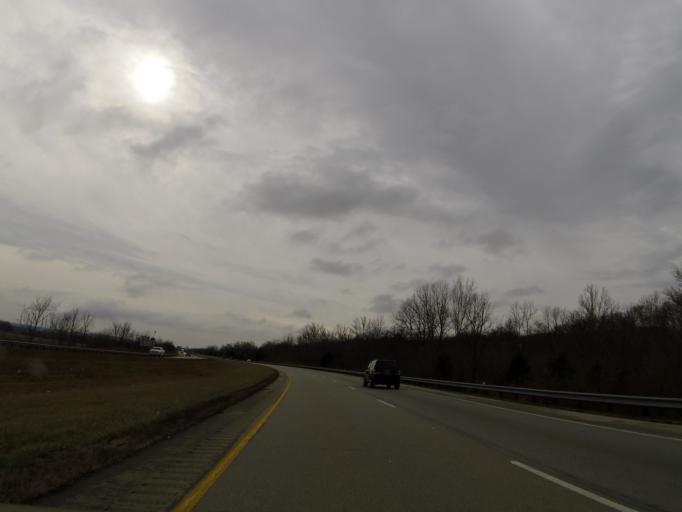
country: US
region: Indiana
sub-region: Dearborn County
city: Hidden Valley
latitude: 39.1818
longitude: -84.7977
